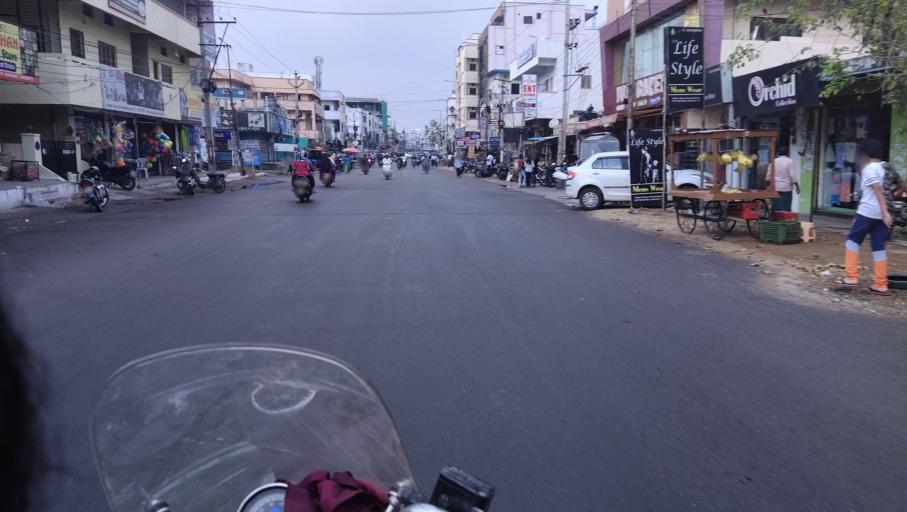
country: IN
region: Telangana
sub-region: Rangareddi
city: Lal Bahadur Nagar
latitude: 17.3212
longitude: 78.5636
